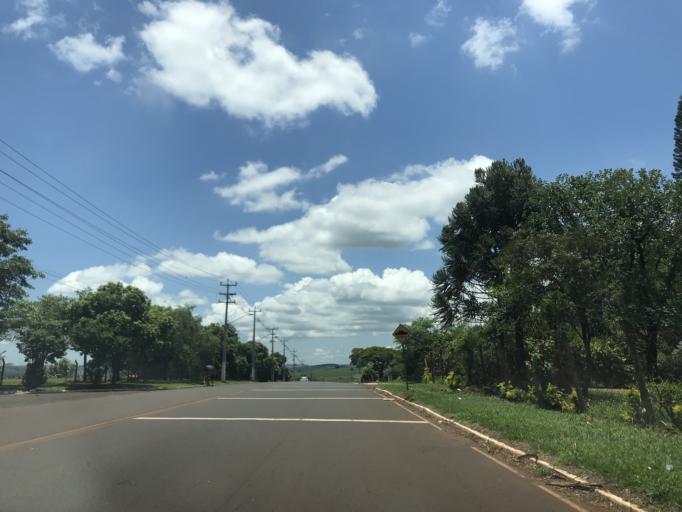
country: BR
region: Parana
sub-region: Marialva
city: Marialva
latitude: -23.4939
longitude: -51.7819
